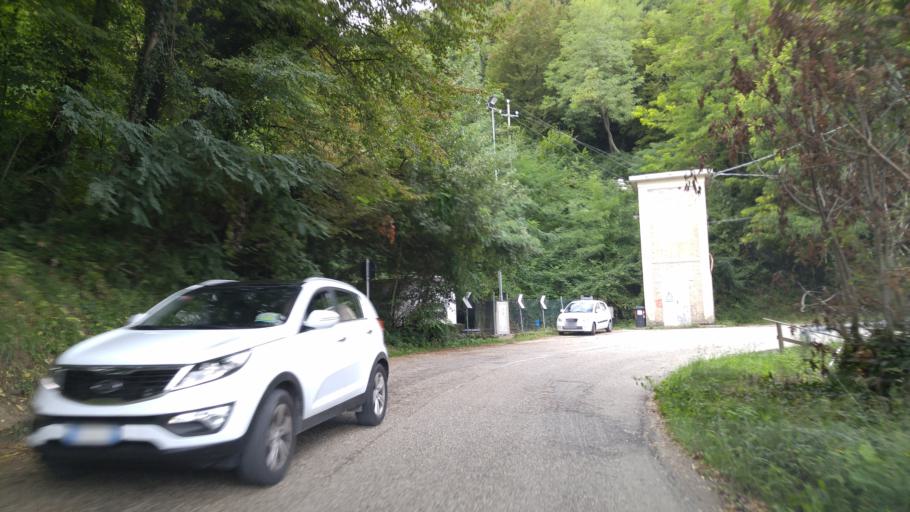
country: IT
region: The Marches
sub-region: Provincia di Pesaro e Urbino
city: Mombaroccio
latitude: 43.7932
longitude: 12.8659
